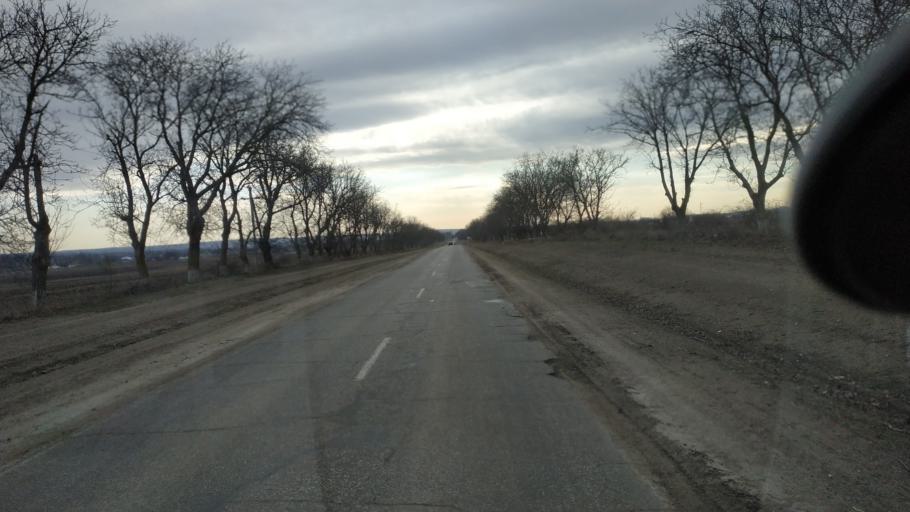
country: MD
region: Criuleni
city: Criuleni
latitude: 47.1749
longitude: 29.1315
